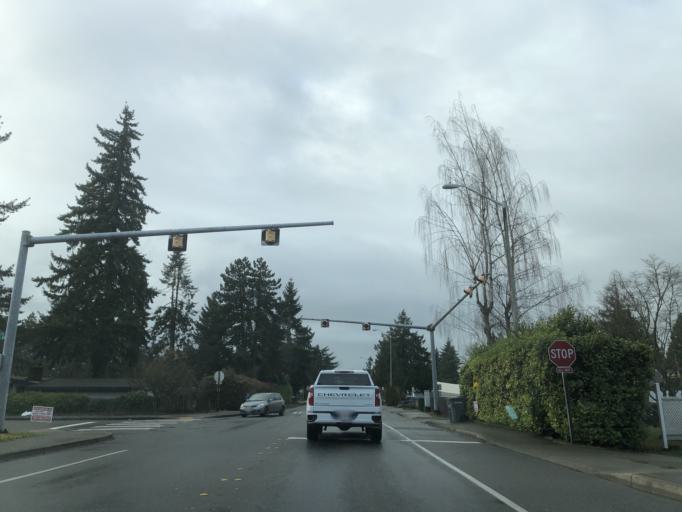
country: US
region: Washington
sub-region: King County
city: SeaTac
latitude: 47.4452
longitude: -122.2810
